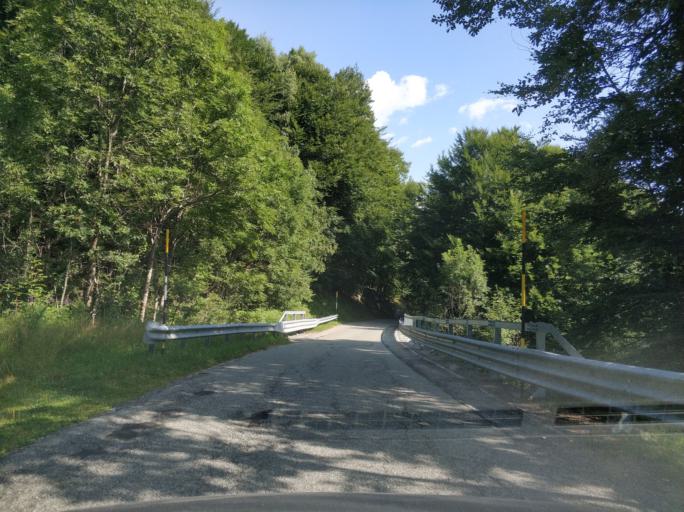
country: IT
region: Piedmont
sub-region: Provincia di Torino
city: Viu
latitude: 45.1874
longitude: 7.3654
